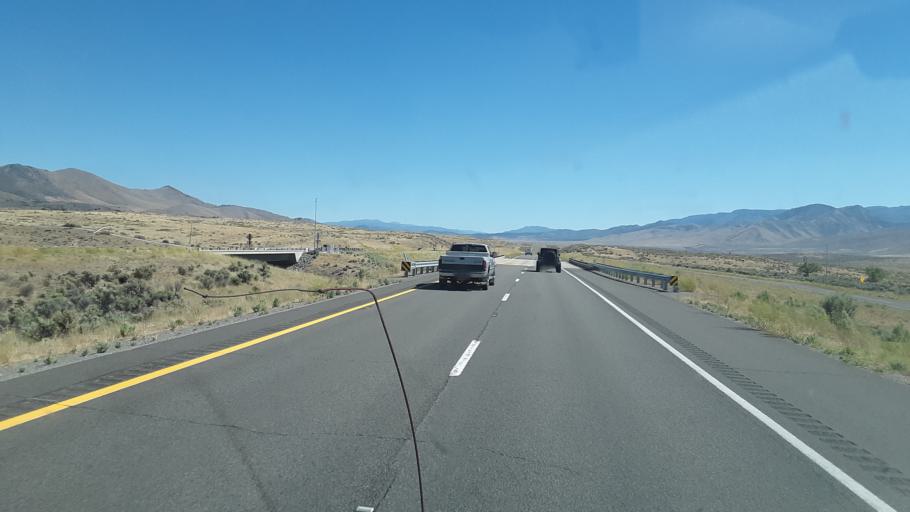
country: US
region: Nevada
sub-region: Washoe County
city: Cold Springs
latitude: 39.7764
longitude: -120.0391
